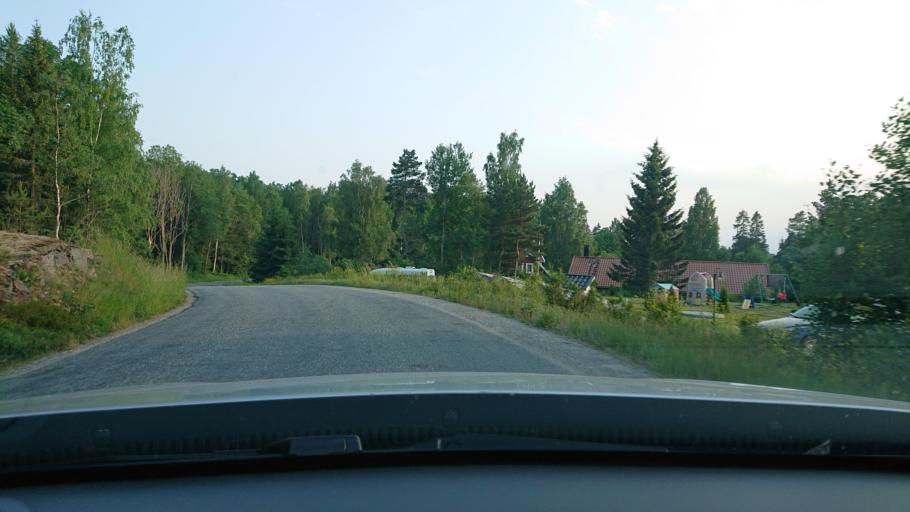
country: SE
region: Stockholm
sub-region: Osterakers Kommun
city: Akersberga
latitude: 59.5139
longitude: 18.3182
